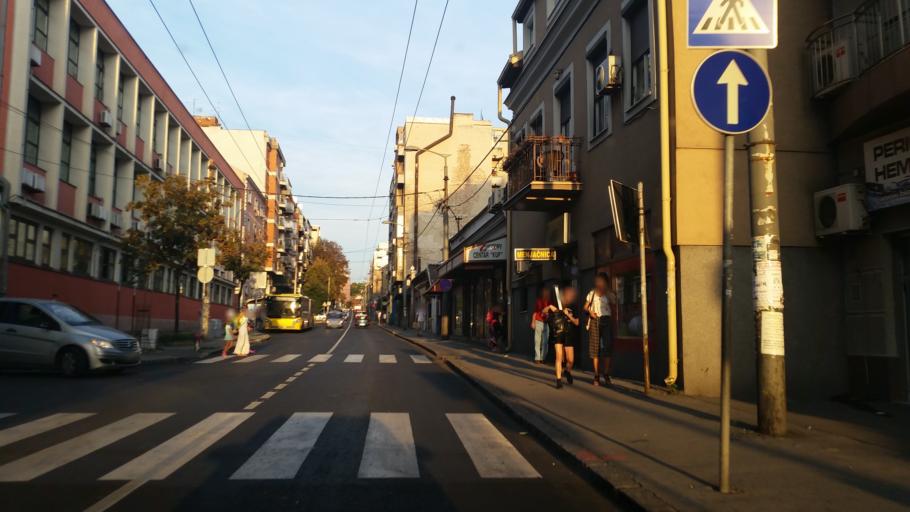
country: RS
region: Central Serbia
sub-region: Belgrade
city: Vracar
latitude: 44.7980
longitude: 20.4794
